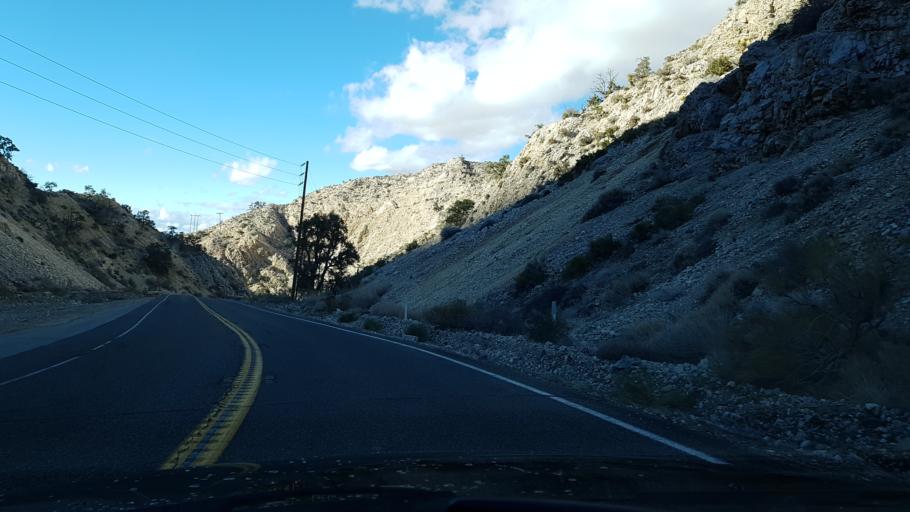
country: US
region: California
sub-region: San Bernardino County
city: Big Bear City
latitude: 34.3457
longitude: -116.8423
